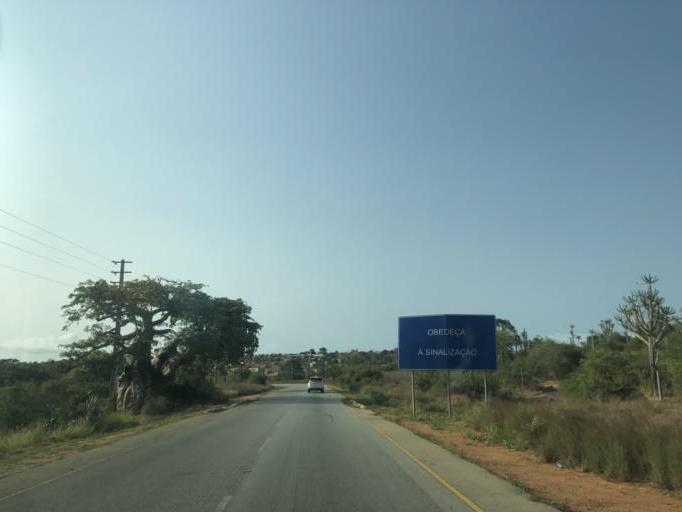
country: AO
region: Luanda
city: Luanda
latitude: -9.2966
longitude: 13.1343
